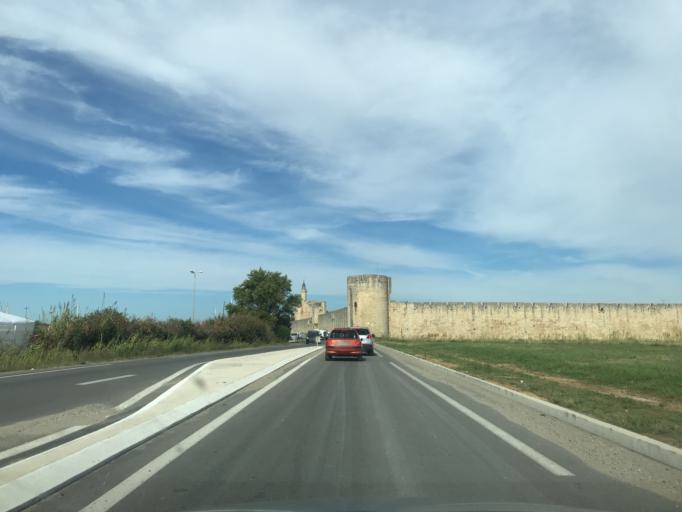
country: FR
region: Languedoc-Roussillon
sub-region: Departement du Gard
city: Aigues-Mortes
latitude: 43.5650
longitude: 4.1864
